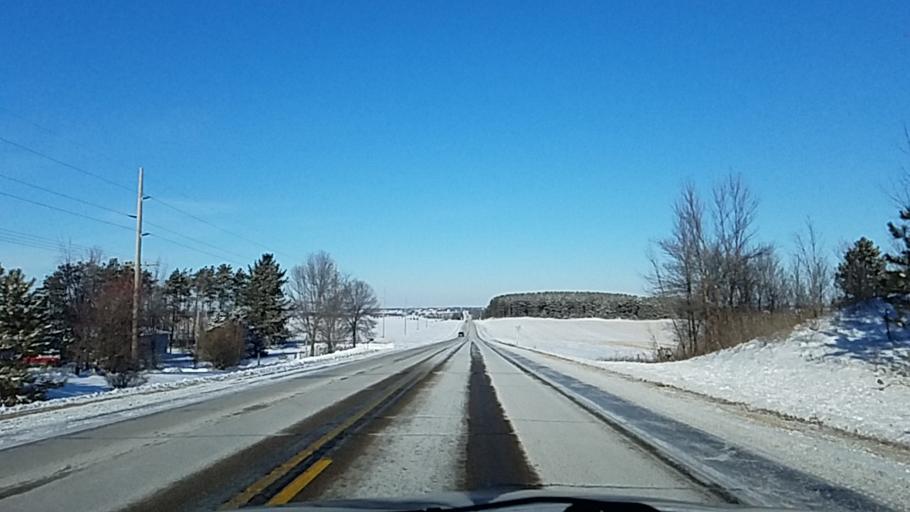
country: US
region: Wisconsin
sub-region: Saint Croix County
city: Roberts
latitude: 45.0275
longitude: -92.5376
